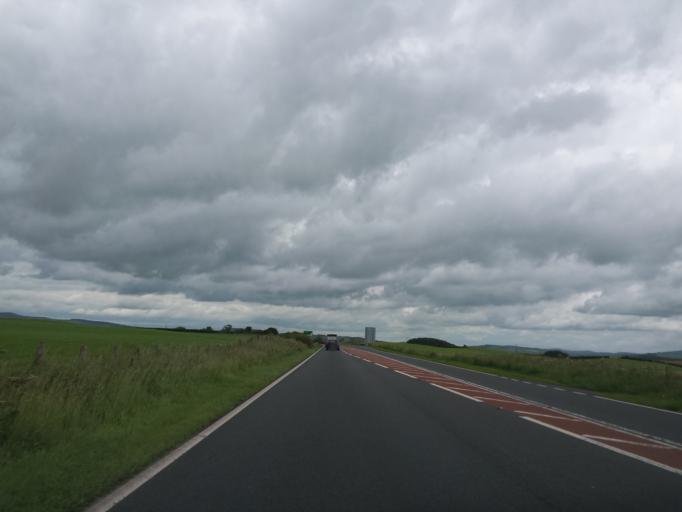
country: GB
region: Scotland
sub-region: Dumfries and Galloway
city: Castle Douglas
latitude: 54.9616
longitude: -3.9118
